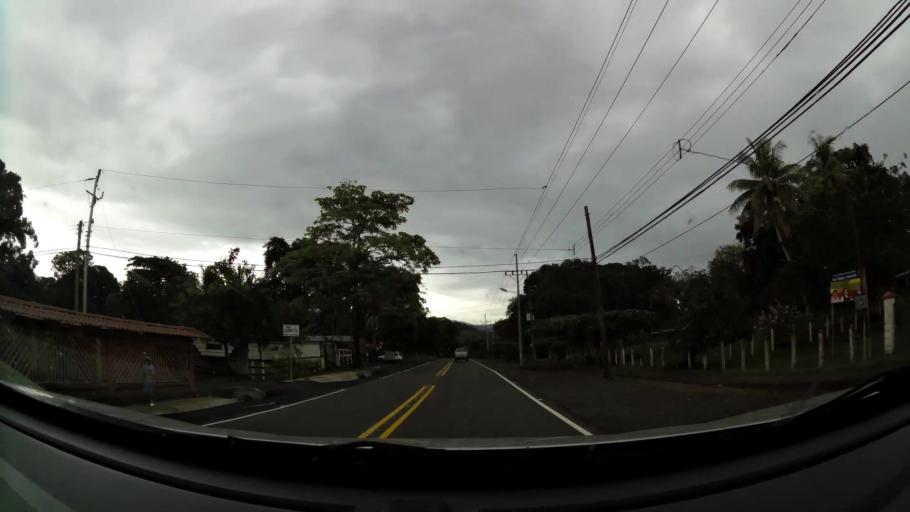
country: CR
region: Alajuela
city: Orotina
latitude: 9.9447
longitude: -84.5476
